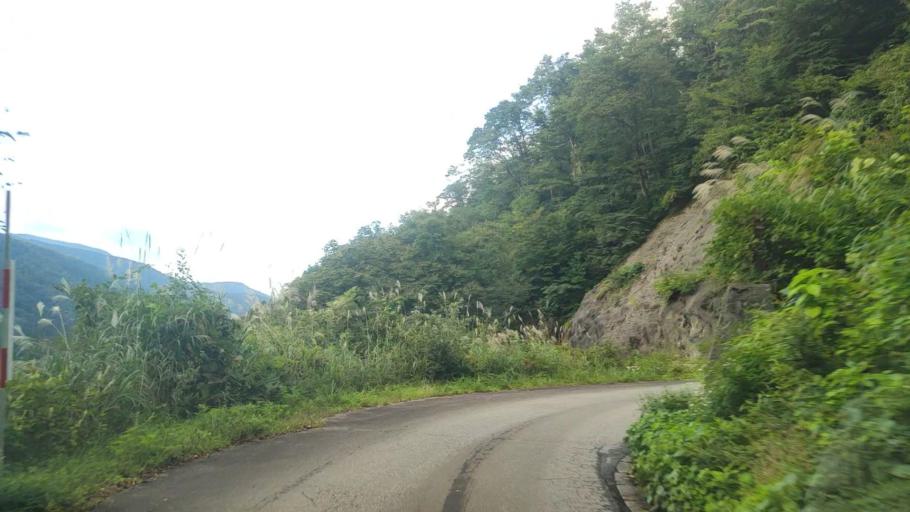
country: JP
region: Toyama
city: Yatsuomachi-higashikumisaka
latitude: 36.4217
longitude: 137.0835
